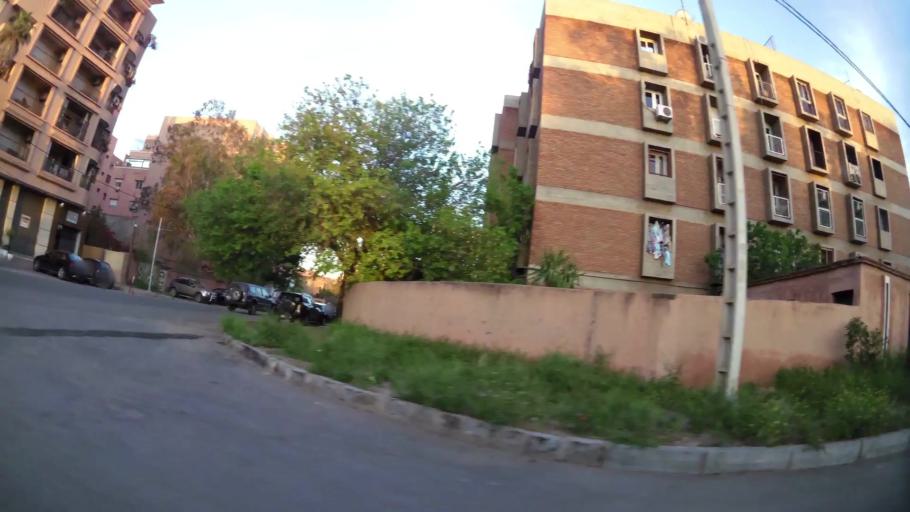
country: MA
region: Marrakech-Tensift-Al Haouz
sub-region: Marrakech
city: Marrakesh
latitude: 31.6389
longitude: -8.0243
